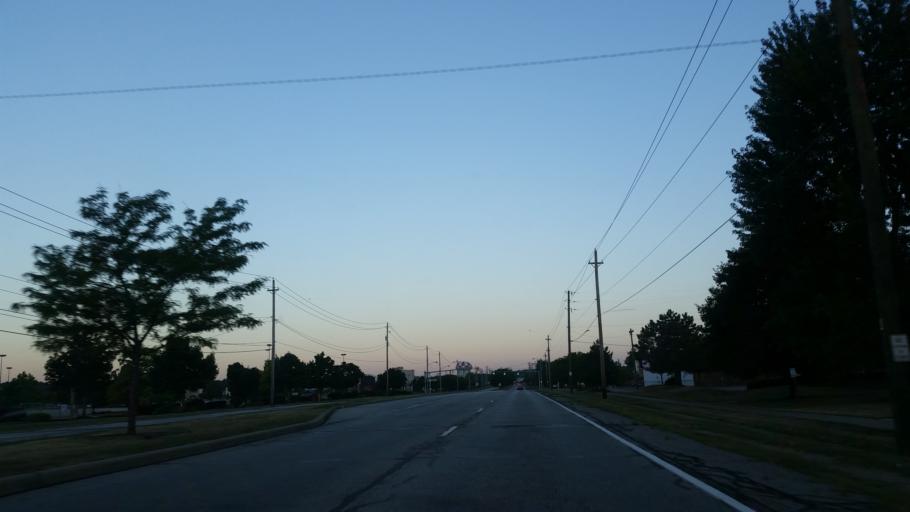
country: US
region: Ohio
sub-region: Cuyahoga County
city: North Olmsted
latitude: 41.4190
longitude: -81.9068
